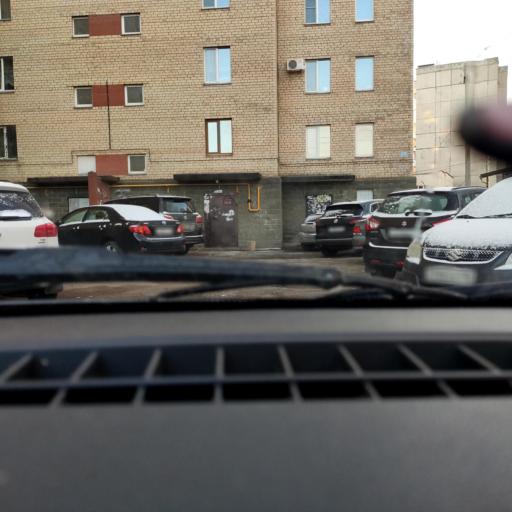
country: RU
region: Bashkortostan
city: Ufa
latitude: 54.7924
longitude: 56.0468
